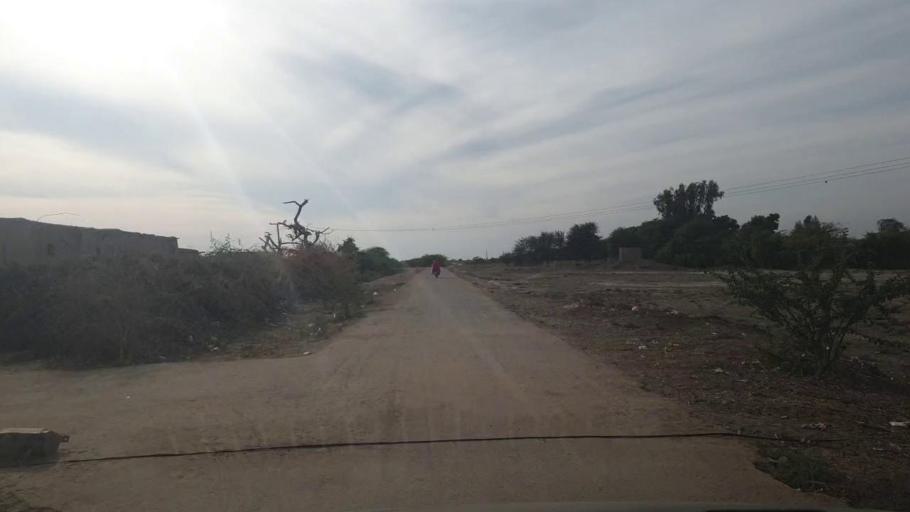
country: PK
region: Sindh
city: Kunri
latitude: 25.2878
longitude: 69.5615
